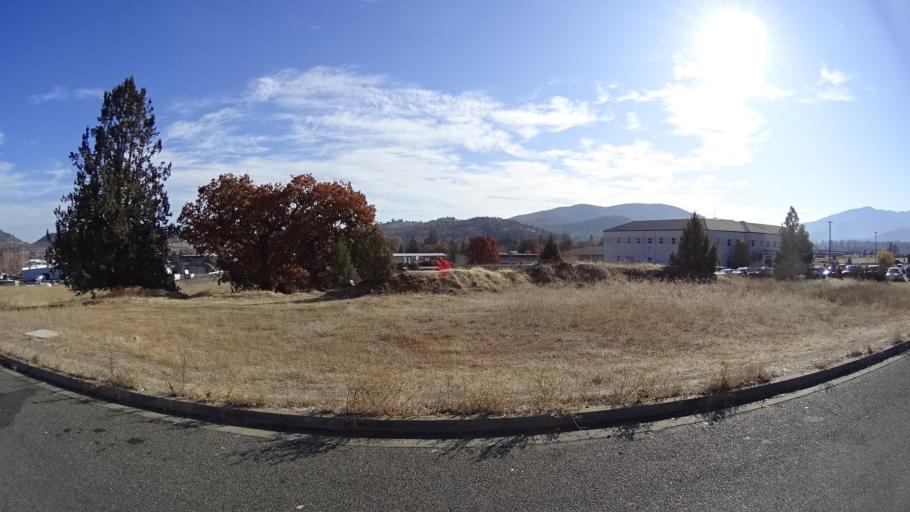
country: US
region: California
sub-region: Siskiyou County
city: Yreka
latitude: 41.7057
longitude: -122.6481
